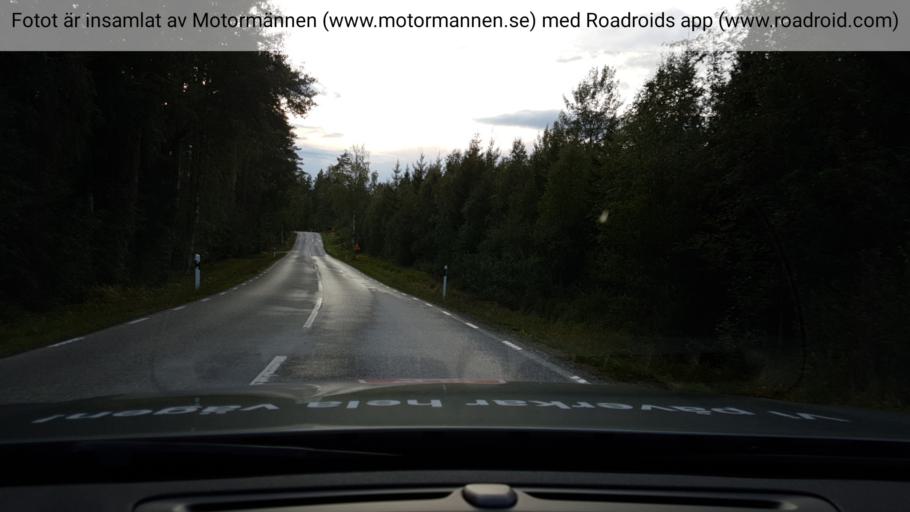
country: SE
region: OErebro
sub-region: Ljusnarsbergs Kommun
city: Kopparberg
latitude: 59.8064
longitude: 14.8462
